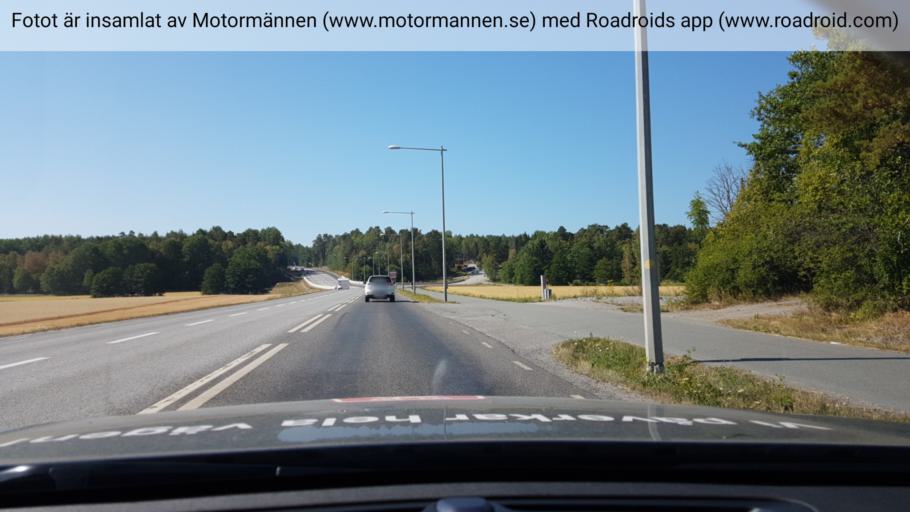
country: SE
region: Stockholm
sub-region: Ekero Kommun
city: Ekeroe
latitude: 59.3168
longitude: 17.8630
